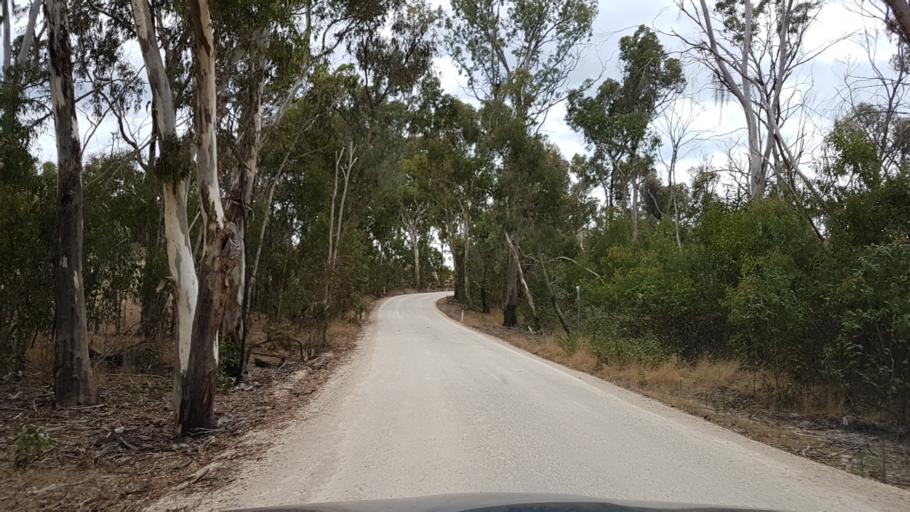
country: AU
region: South Australia
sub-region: Adelaide Hills
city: Gumeracha
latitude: -34.7851
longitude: 138.8373
